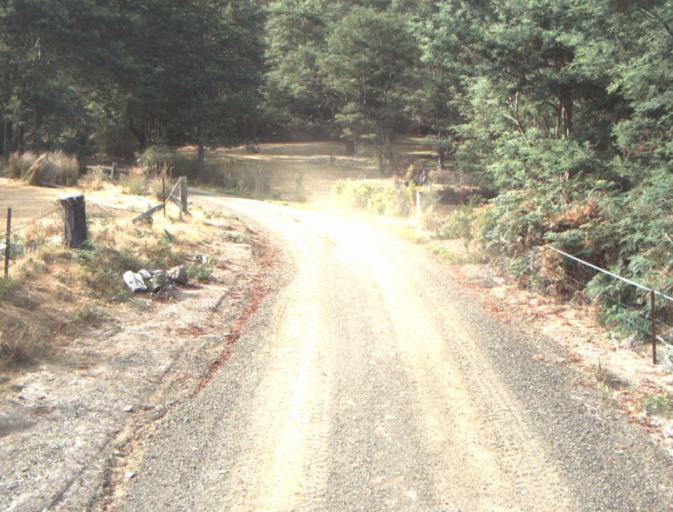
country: AU
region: Tasmania
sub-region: Launceston
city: Mayfield
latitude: -41.2941
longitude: 147.2176
